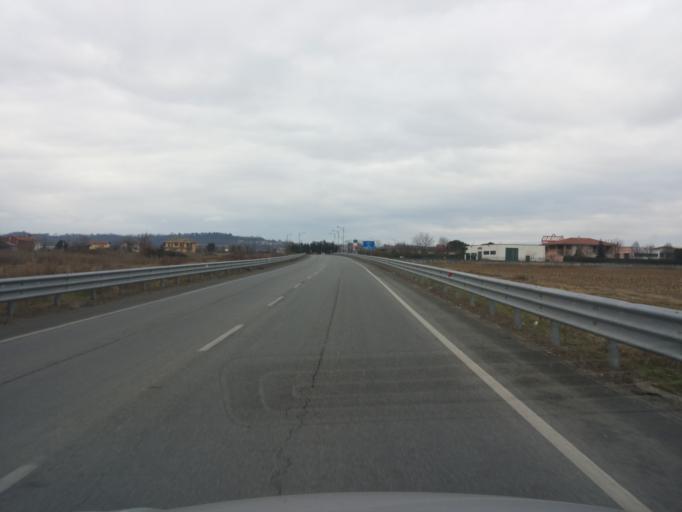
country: IT
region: Piedmont
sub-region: Provincia di Vercelli
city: Cigliano
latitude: 45.3157
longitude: 8.0331
